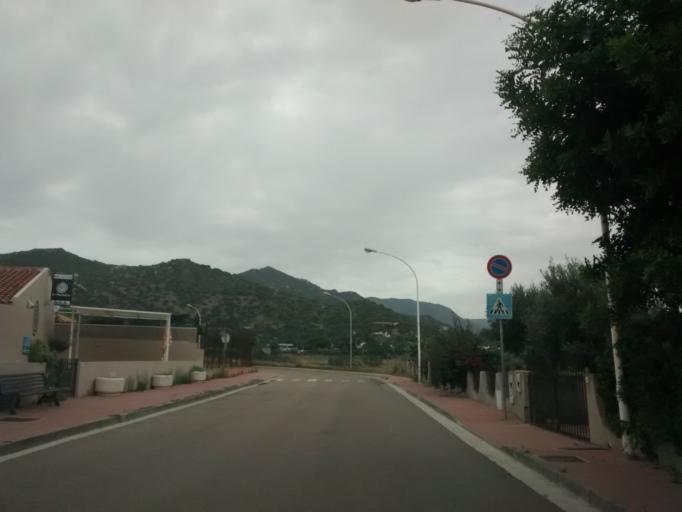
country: IT
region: Sardinia
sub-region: Provincia di Cagliari
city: Villasimius
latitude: 39.1381
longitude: 9.4309
